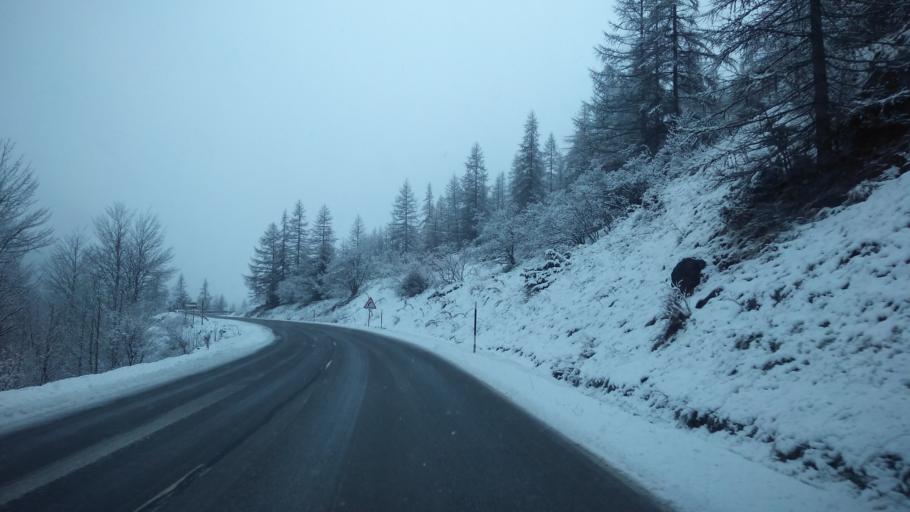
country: FR
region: Provence-Alpes-Cote d'Azur
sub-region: Departement des Hautes-Alpes
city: Le Monetier-les-Bains
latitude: 44.9951
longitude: 6.4801
